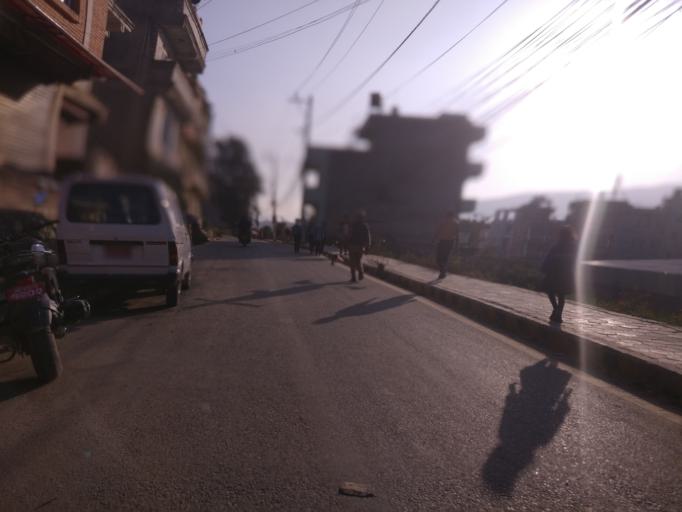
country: NP
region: Central Region
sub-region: Bagmati Zone
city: Patan
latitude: 27.6557
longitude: 85.3154
